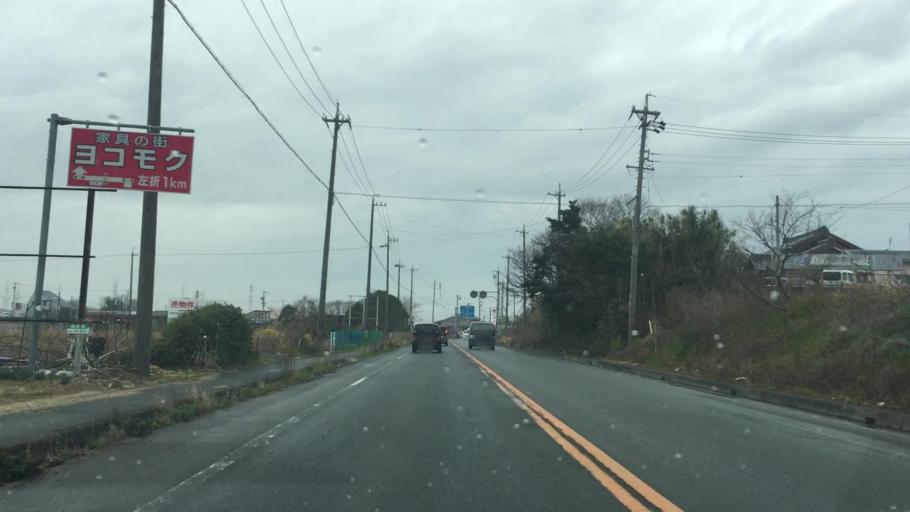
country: JP
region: Aichi
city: Toyohashi
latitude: 34.7148
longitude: 137.3902
